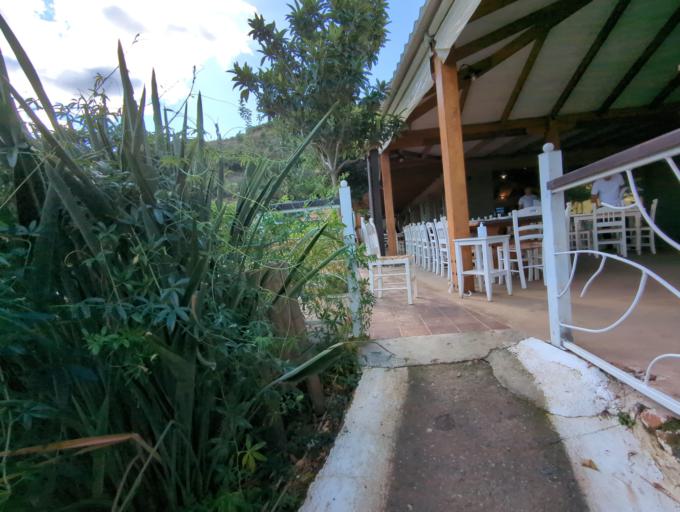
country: GR
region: Crete
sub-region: Nomos Chanias
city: Galatas
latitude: 35.4187
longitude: 23.9396
